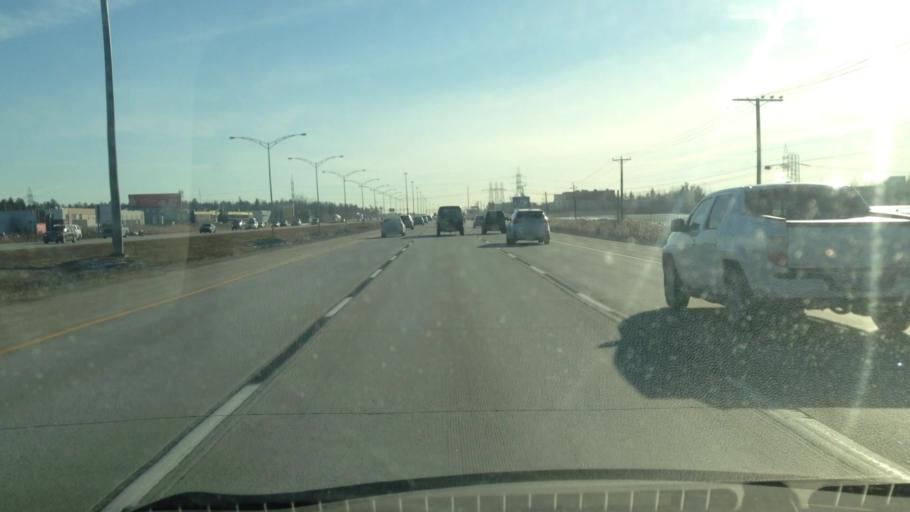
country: CA
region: Quebec
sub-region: Laurentides
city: Blainville
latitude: 45.6884
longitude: -73.9312
